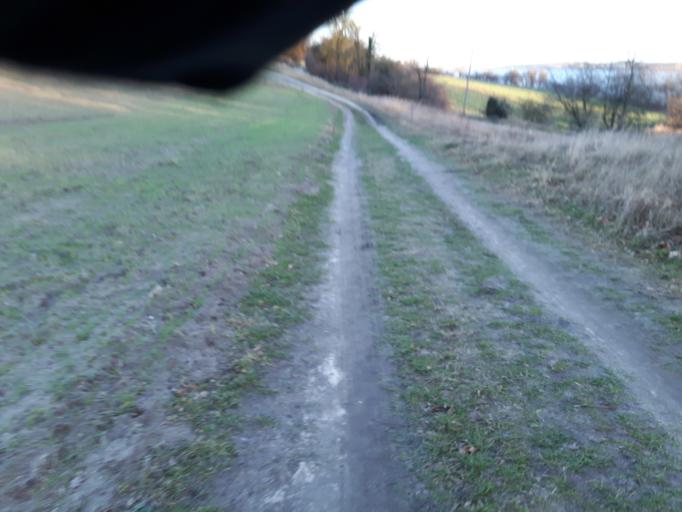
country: DE
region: Mecklenburg-Vorpommern
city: Ostseebad Binz
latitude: 54.3188
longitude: 13.6155
